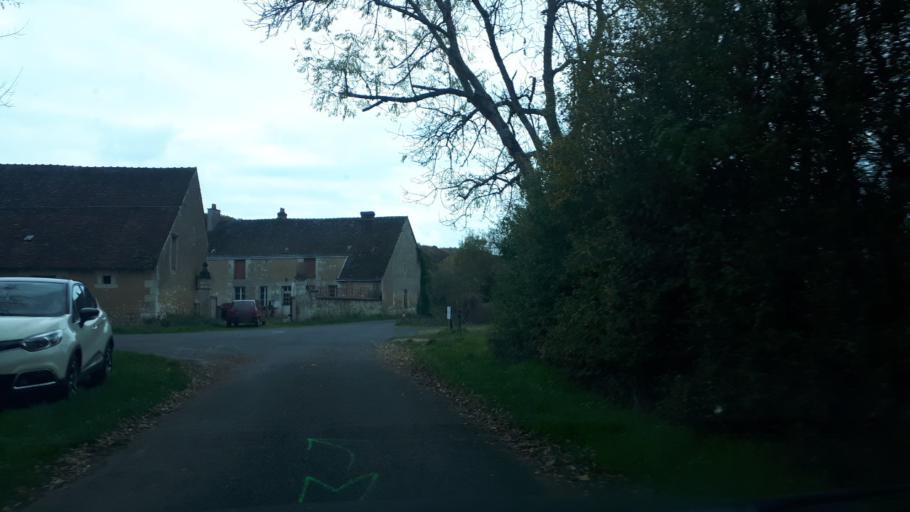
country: FR
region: Centre
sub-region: Departement du Loir-et-Cher
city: Lunay
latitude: 47.7709
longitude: 0.9529
